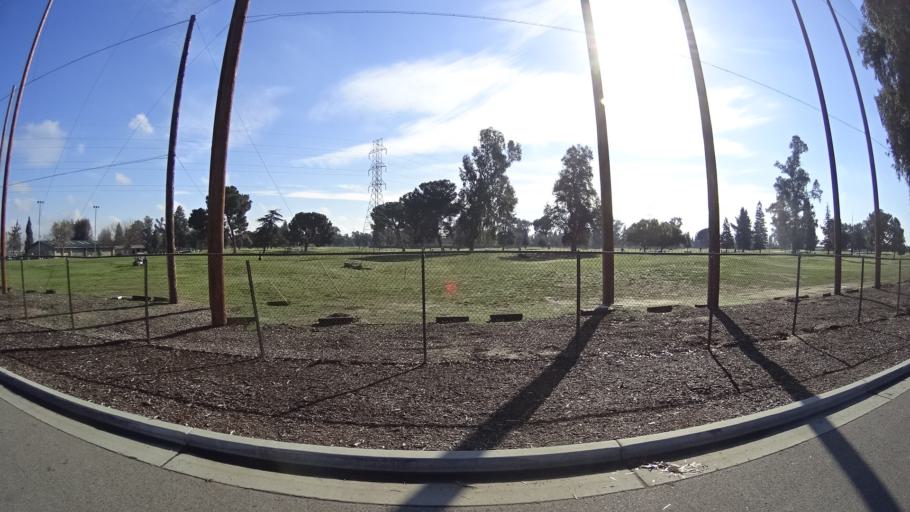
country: US
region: California
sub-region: Fresno County
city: Biola
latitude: 36.8439
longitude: -119.9111
